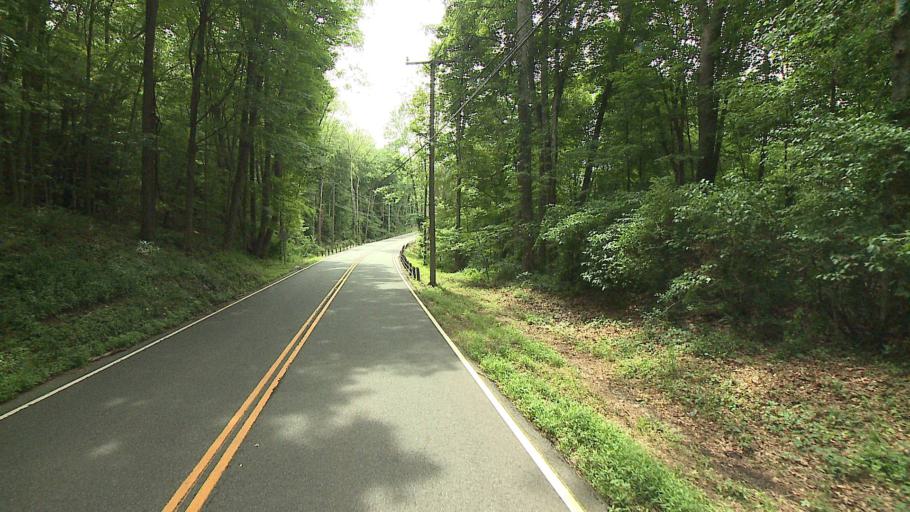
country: US
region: Connecticut
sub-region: Litchfield County
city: New Milford
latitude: 41.5806
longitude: -73.3200
